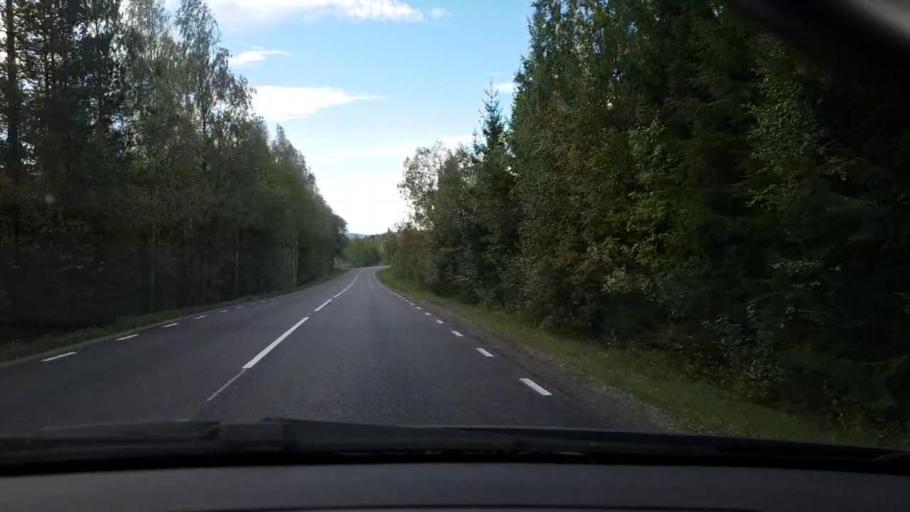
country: SE
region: Dalarna
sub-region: Borlange Kommun
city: Ornas
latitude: 60.5096
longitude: 15.5222
